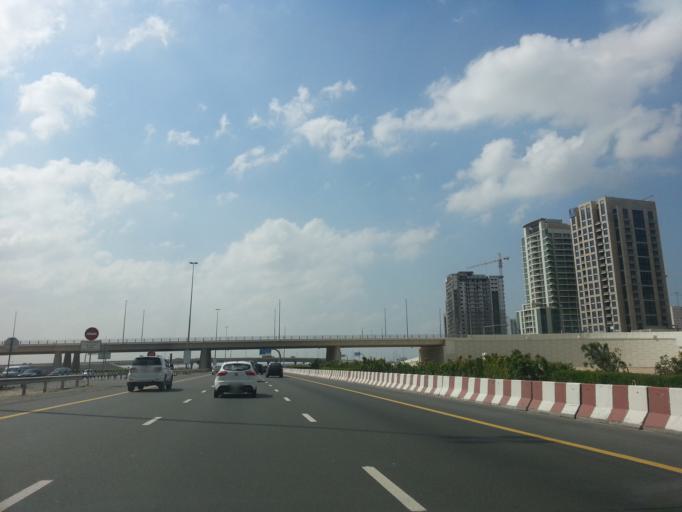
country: AE
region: Dubai
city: Dubai
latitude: 25.1867
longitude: 55.2891
